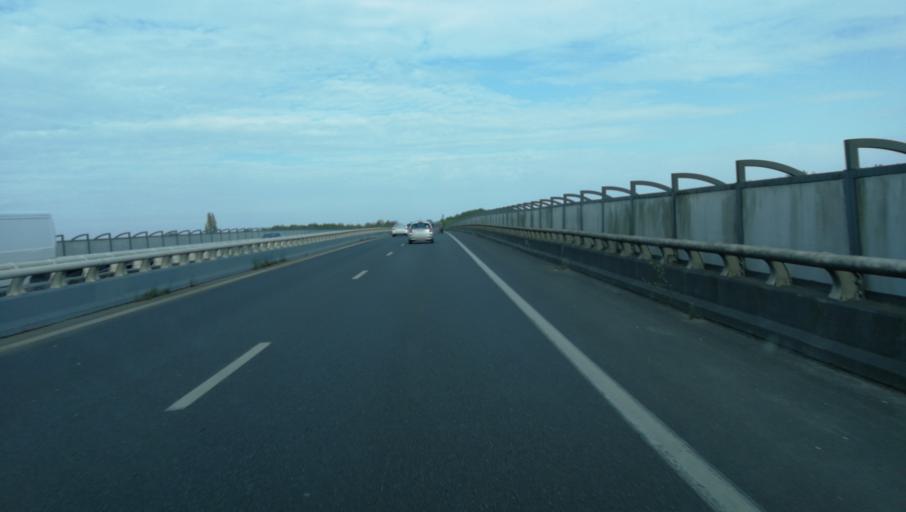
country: FR
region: Pays de la Loire
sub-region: Departement de la Loire-Atlantique
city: La Chapelle-sur-Erdre
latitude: 47.2751
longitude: -1.5294
